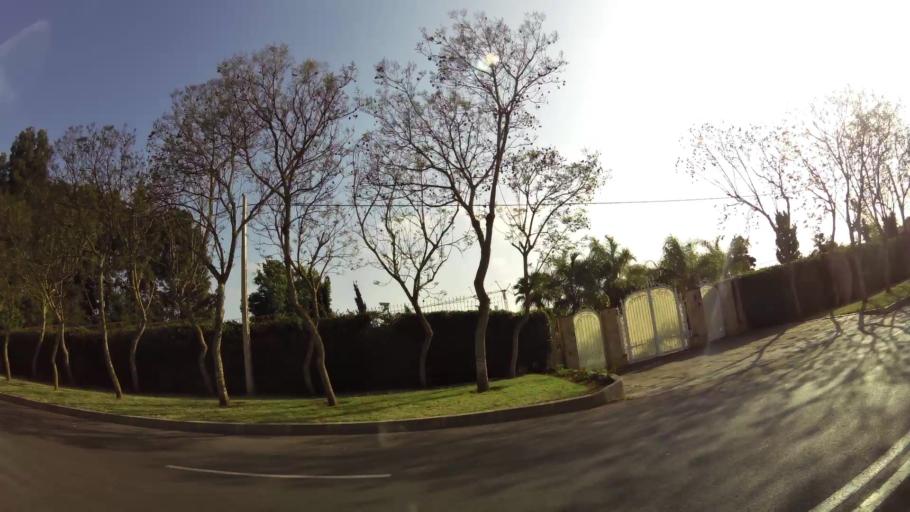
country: MA
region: Rabat-Sale-Zemmour-Zaer
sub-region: Rabat
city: Rabat
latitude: 33.9374
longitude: -6.8182
